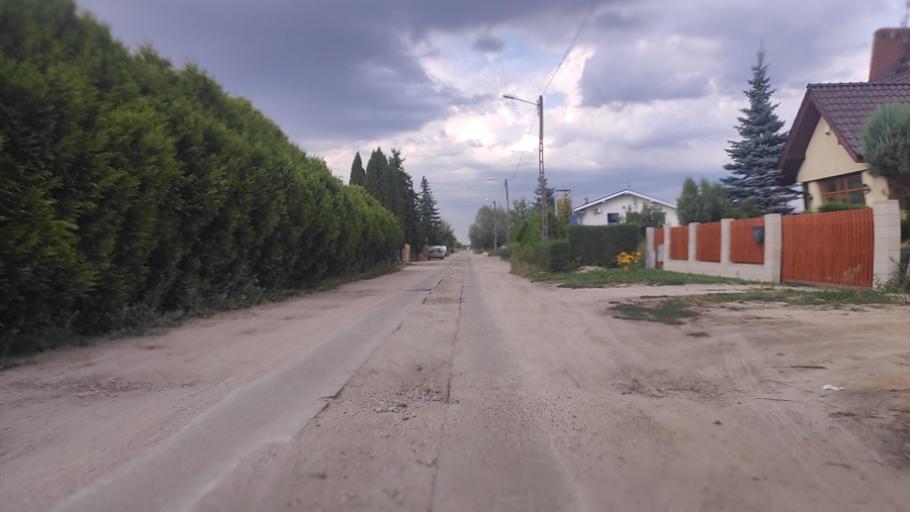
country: PL
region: Greater Poland Voivodeship
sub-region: Powiat poznanski
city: Swarzedz
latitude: 52.4088
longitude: 17.0995
